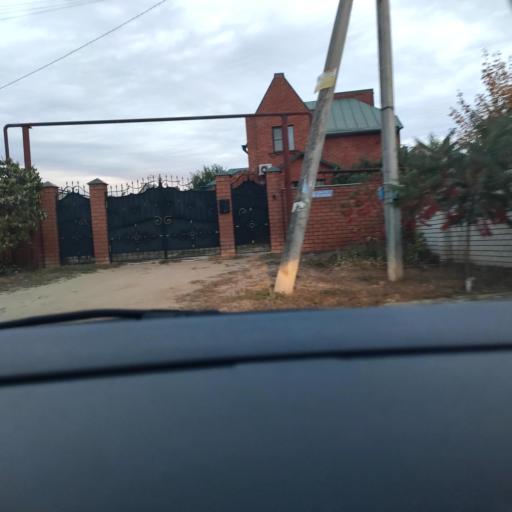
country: RU
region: Voronezj
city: Podgornoye
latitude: 51.7231
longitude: 39.1487
